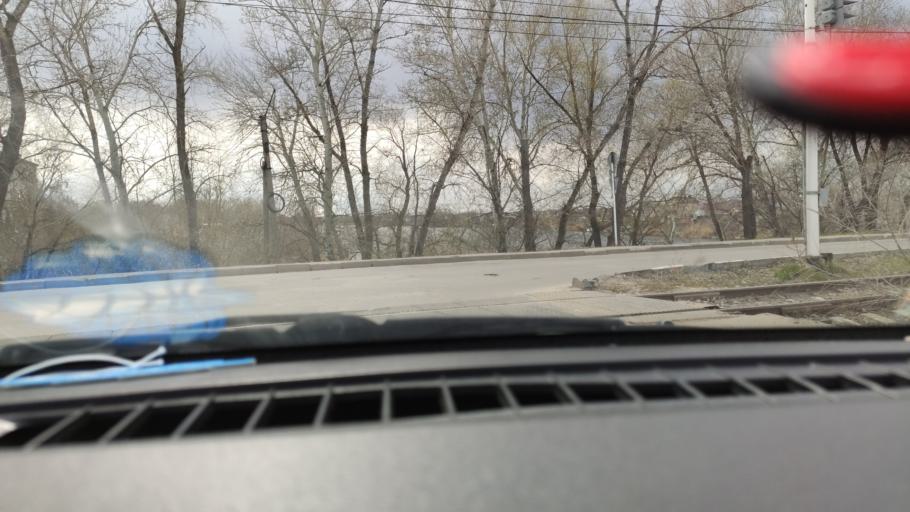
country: RU
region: Saratov
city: Engel's
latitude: 51.5034
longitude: 46.0759
